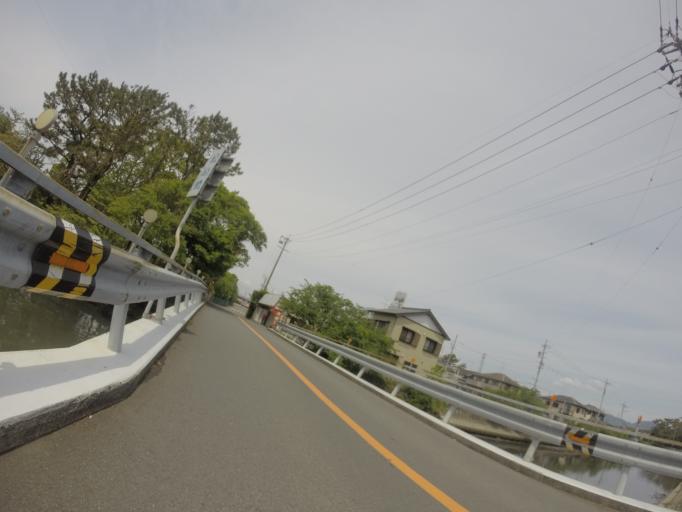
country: JP
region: Shizuoka
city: Yaizu
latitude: 34.8326
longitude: 138.3349
